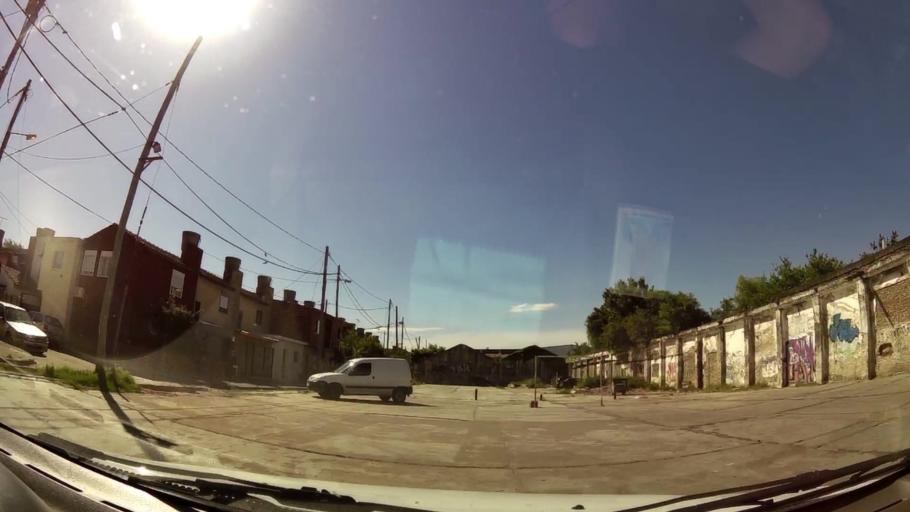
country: AR
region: Buenos Aires
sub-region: Partido de San Isidro
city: San Isidro
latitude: -34.4693
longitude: -58.5317
